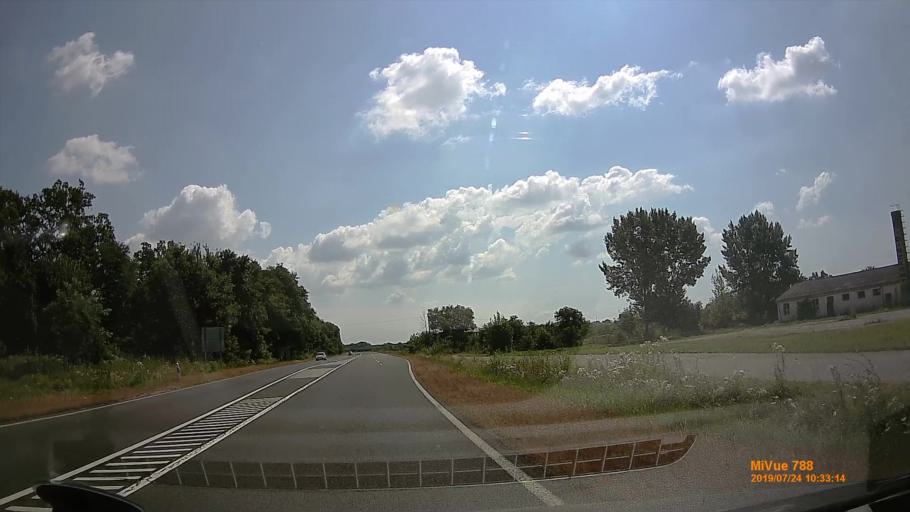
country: HU
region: Szabolcs-Szatmar-Bereg
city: Tarpa
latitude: 48.1589
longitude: 22.5468
